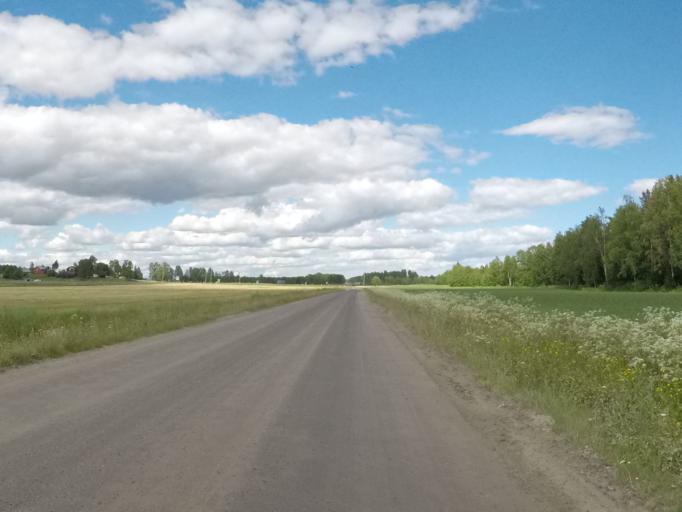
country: SE
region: Vaesterbotten
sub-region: Robertsfors Kommun
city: Robertsfors
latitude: 64.0747
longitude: 20.8658
